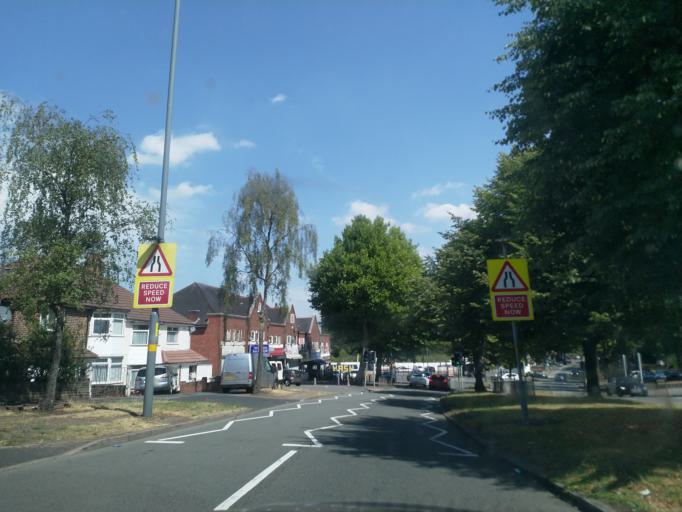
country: GB
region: England
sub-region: Sandwell
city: Smethwick
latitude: 52.5136
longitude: -1.9480
